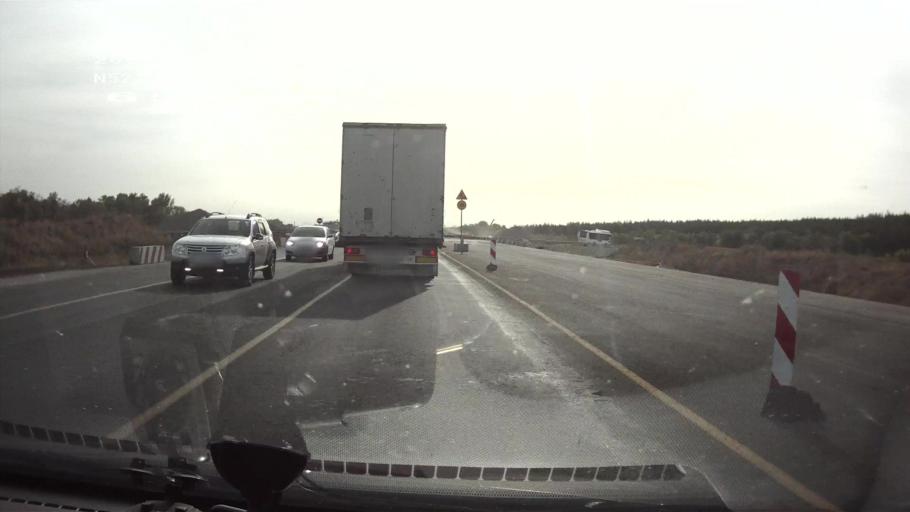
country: RU
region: Saratov
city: Sinodskoye
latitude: 52.0153
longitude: 46.6950
